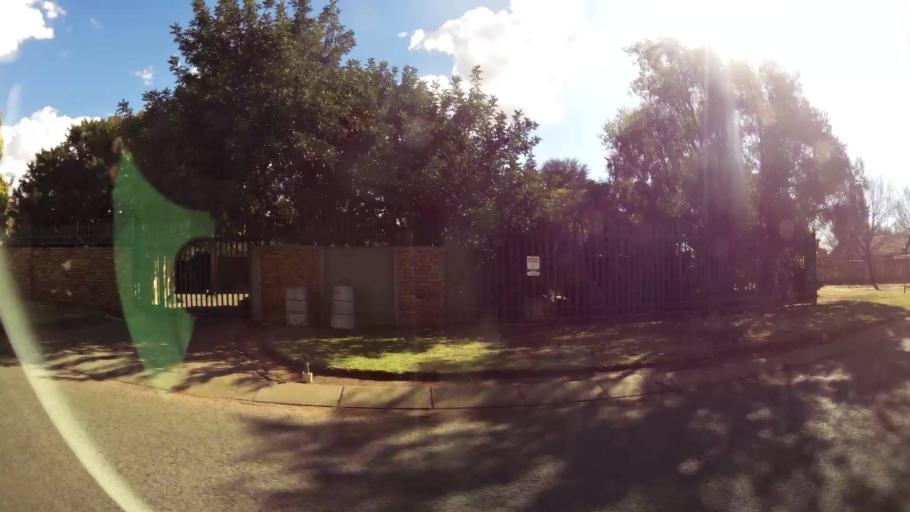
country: ZA
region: North-West
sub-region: Dr Kenneth Kaunda District Municipality
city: Klerksdorp
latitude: -26.8586
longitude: 26.6210
